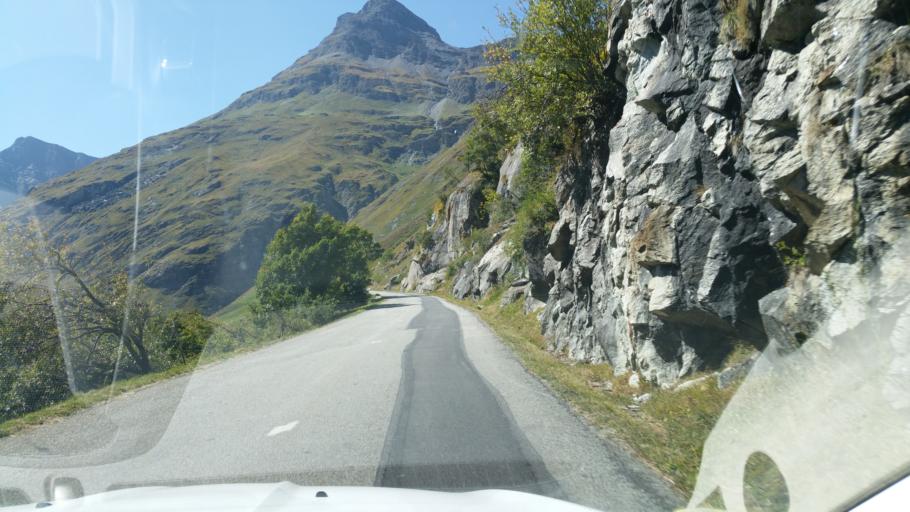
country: FR
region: Rhone-Alpes
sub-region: Departement de la Savoie
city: Val-d'Isere
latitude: 45.3713
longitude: 7.0351
